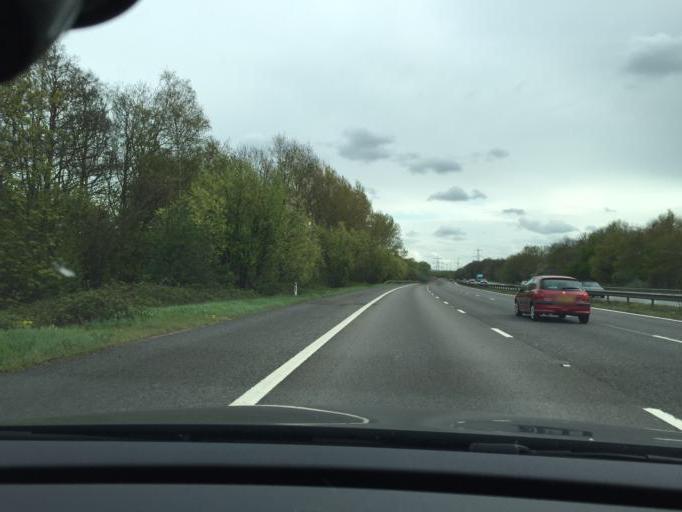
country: GB
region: England
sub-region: West Berkshire
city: Theale
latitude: 51.4491
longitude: -1.0753
